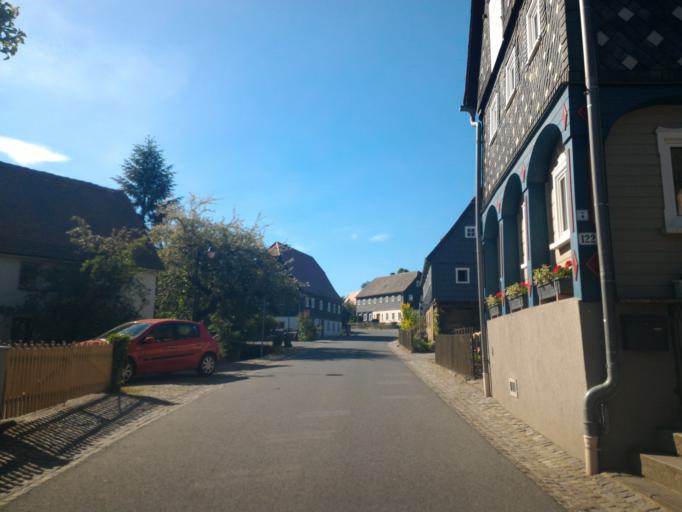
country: DE
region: Saxony
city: Niedercunnersdorf
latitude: 51.0292
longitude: 14.6725
